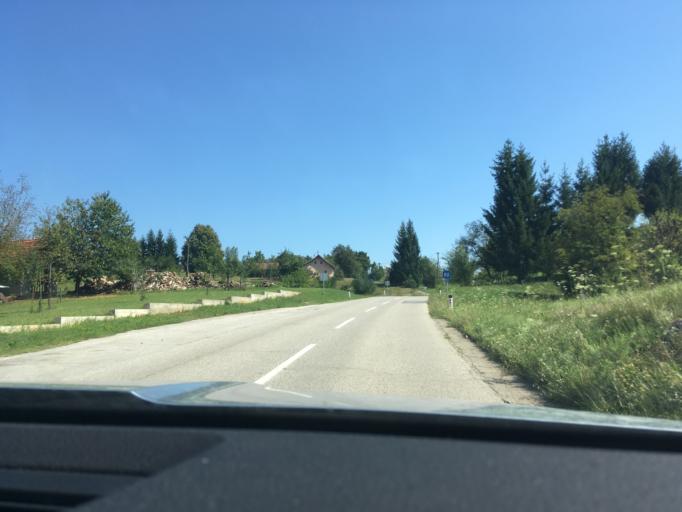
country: SI
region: Metlika
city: Metlika
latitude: 45.5267
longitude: 15.3065
